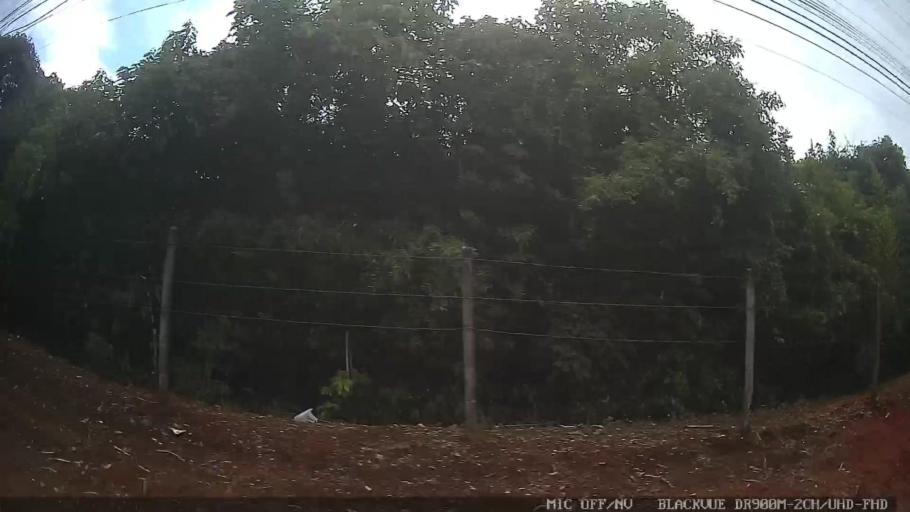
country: BR
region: Sao Paulo
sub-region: Itaquaquecetuba
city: Itaquaquecetuba
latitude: -23.4866
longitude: -46.3123
